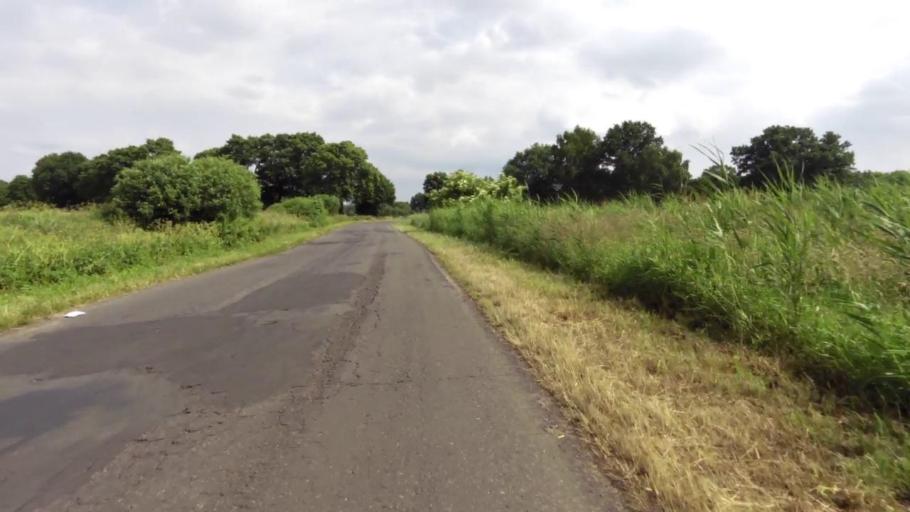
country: PL
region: West Pomeranian Voivodeship
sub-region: Powiat goleniowski
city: Stepnica
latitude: 53.6662
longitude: 14.5928
